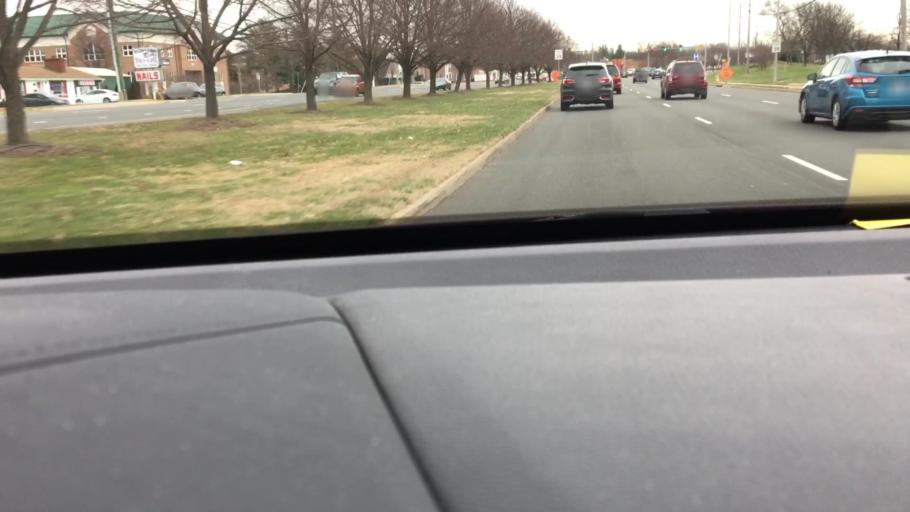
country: US
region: Virginia
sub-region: Prince William County
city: West Gate
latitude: 38.7693
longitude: -77.4895
